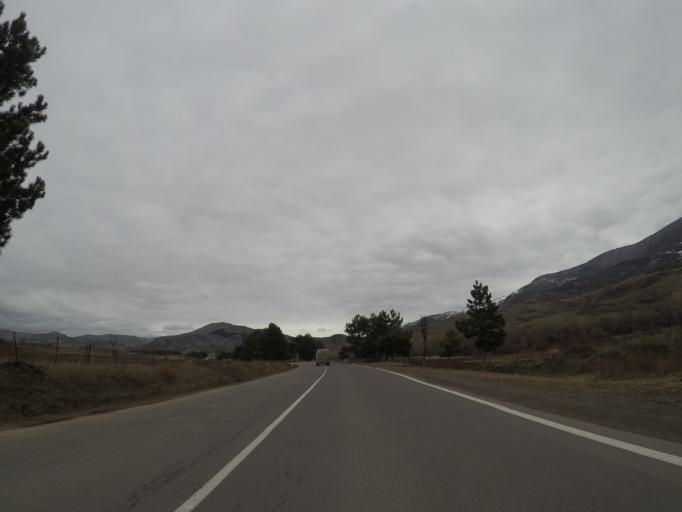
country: GE
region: Samtskhe-Javakheti
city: Akhaltsikhe
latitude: 41.6159
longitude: 43.1163
